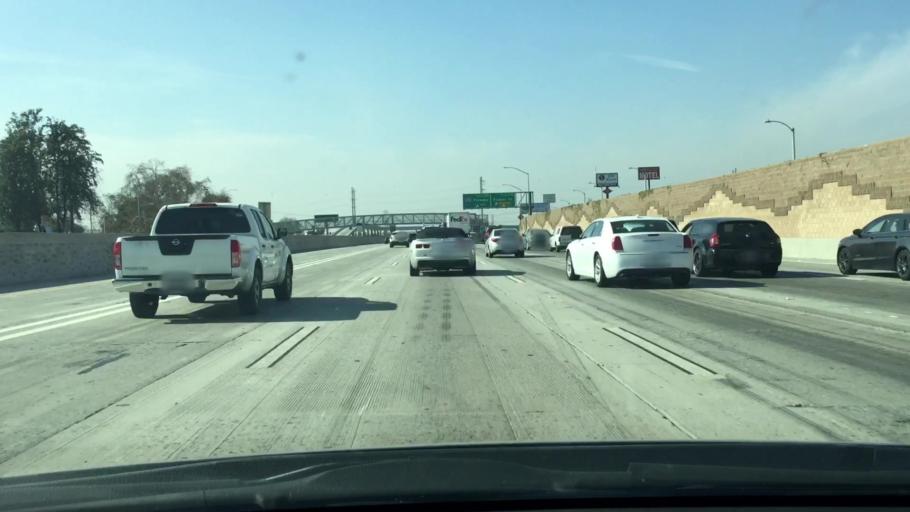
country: US
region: California
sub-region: Los Angeles County
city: West Puente Valley
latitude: 34.0671
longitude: -117.9866
